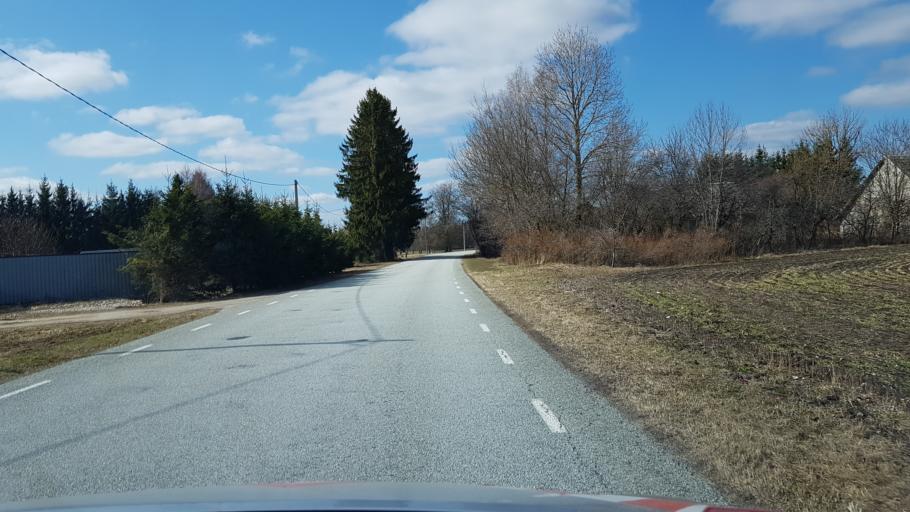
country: EE
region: Laeaene-Virumaa
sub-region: Tapa vald
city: Tapa
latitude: 59.2515
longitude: 25.7433
